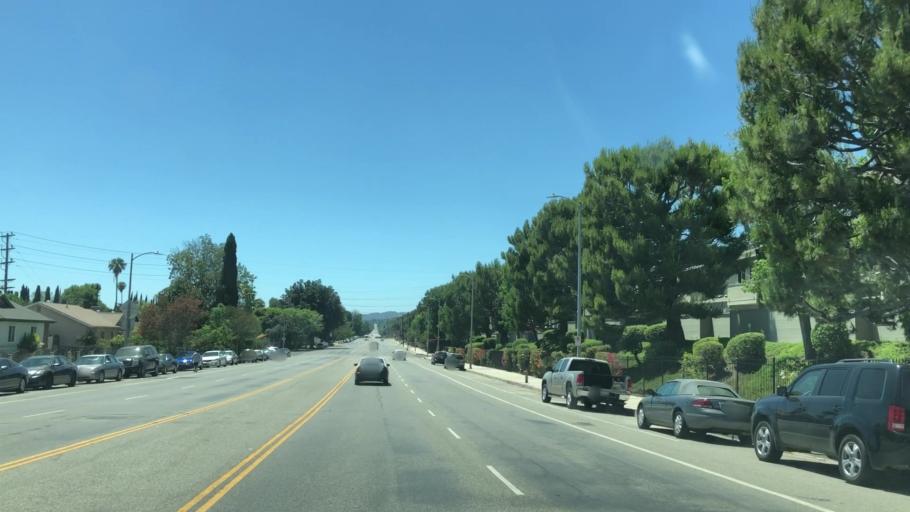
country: US
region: California
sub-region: Los Angeles County
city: San Fernando
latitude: 34.2791
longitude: -118.4723
